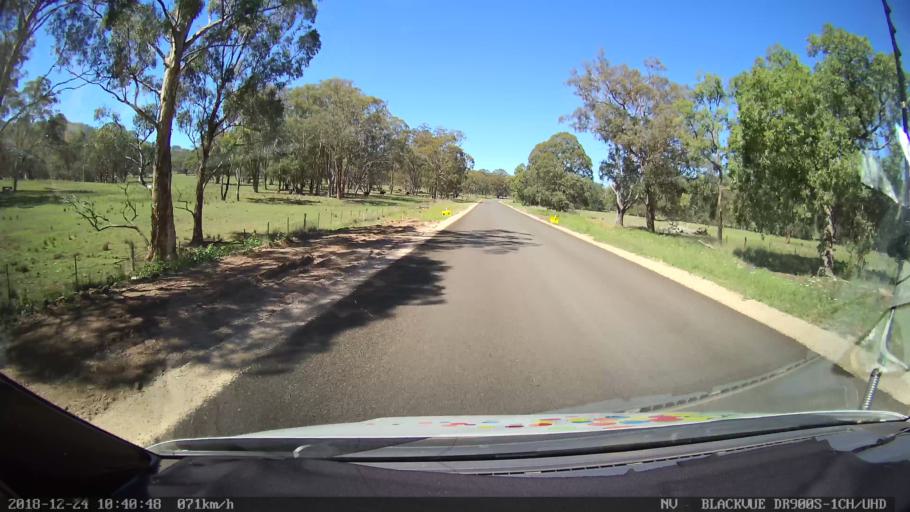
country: AU
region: New South Wales
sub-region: Upper Hunter Shire
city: Merriwa
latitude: -31.8643
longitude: 150.4643
